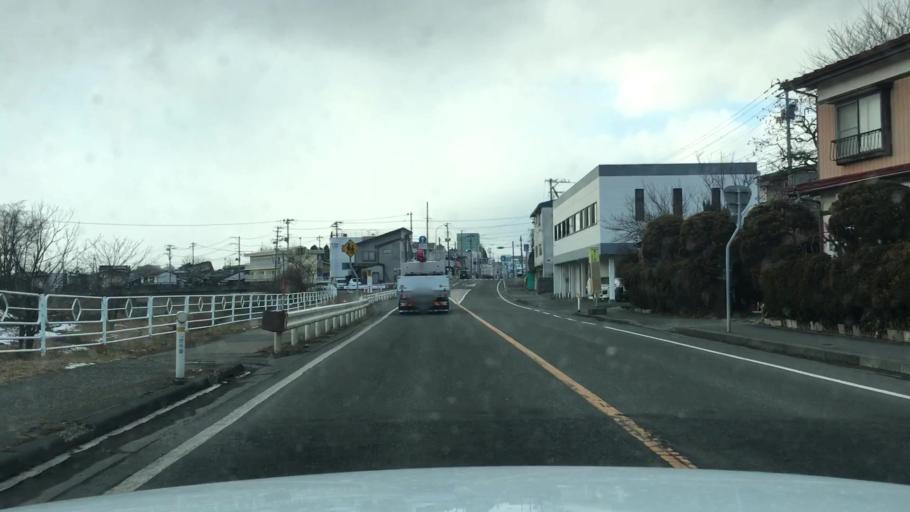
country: JP
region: Iwate
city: Morioka-shi
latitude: 39.6905
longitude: 141.1744
